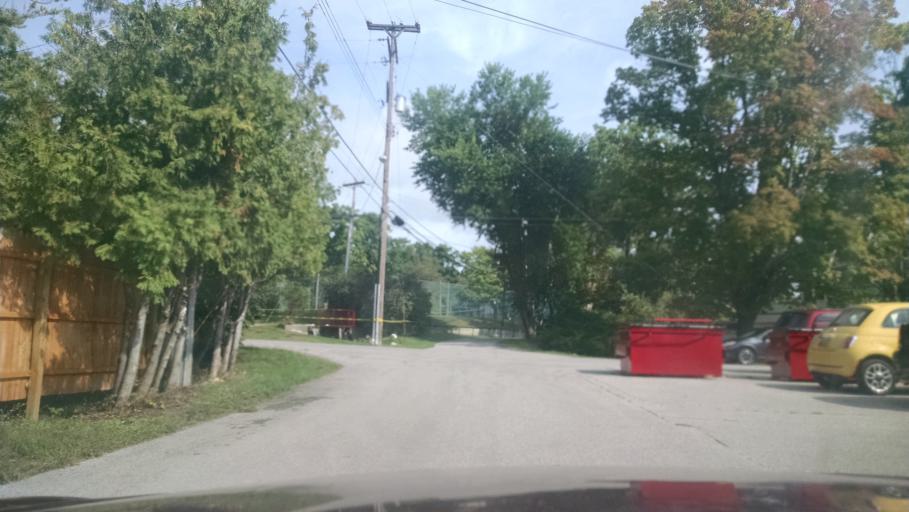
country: US
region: Michigan
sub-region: Leelanau County
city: Leland
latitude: 44.9767
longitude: -85.6518
